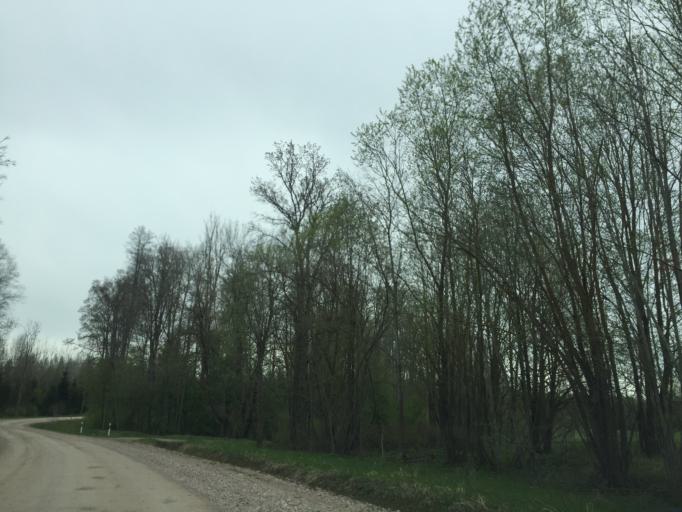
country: LV
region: Lecava
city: Iecava
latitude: 56.6345
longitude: 24.1836
